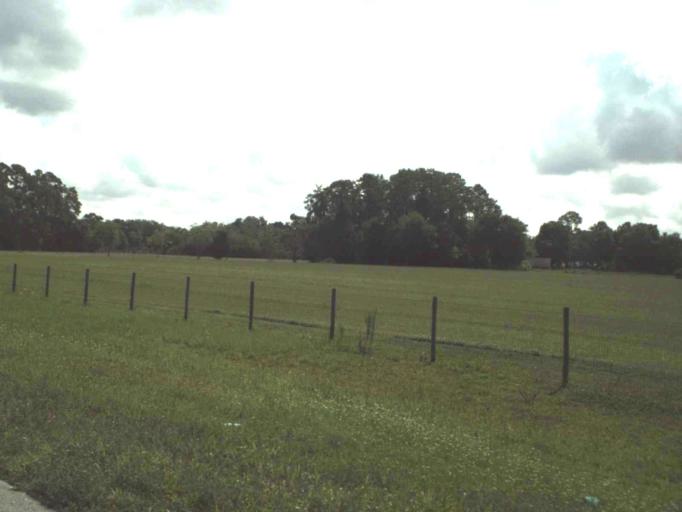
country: US
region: Florida
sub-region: Volusia County
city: Samsula-Spruce Creek
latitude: 28.9479
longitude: -81.0991
